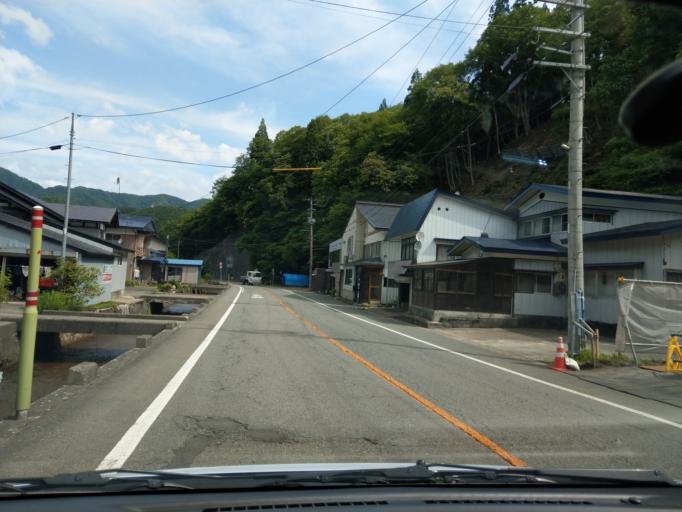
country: JP
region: Akita
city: Kakunodatemachi
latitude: 39.7319
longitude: 140.5829
